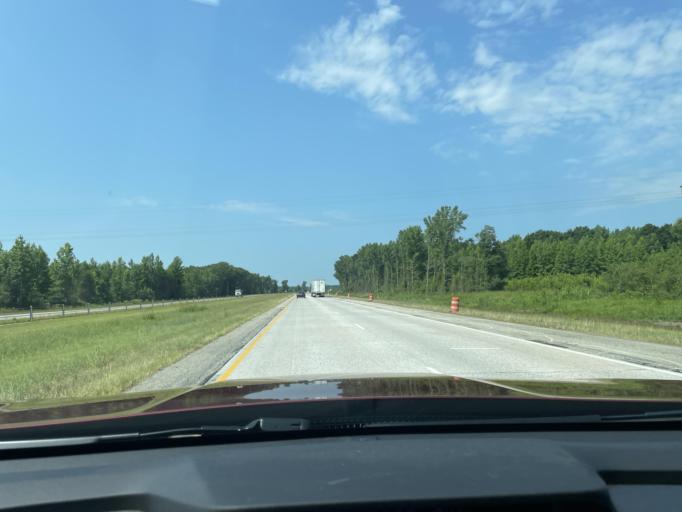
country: US
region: Arkansas
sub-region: White County
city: Searcy
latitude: 35.1553
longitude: -91.7873
